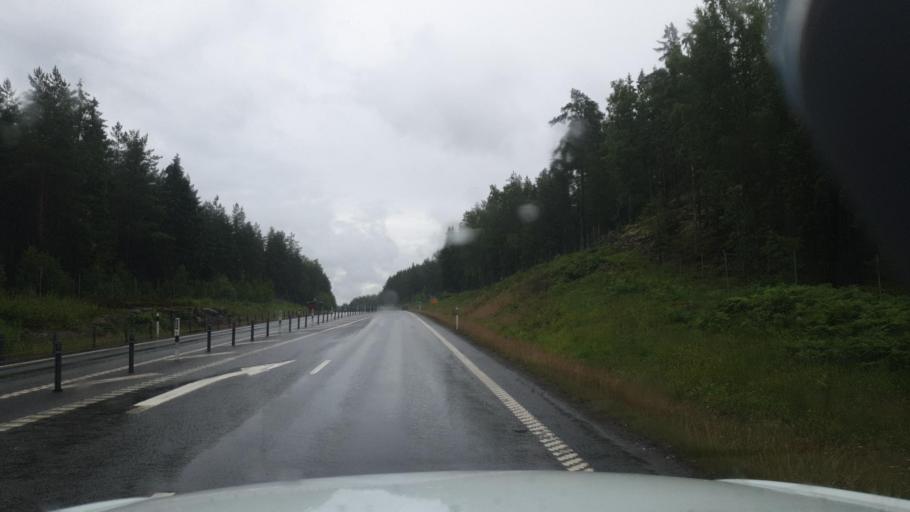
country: SE
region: Vaermland
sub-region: Arvika Kommun
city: Arvika
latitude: 59.6472
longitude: 12.6893
